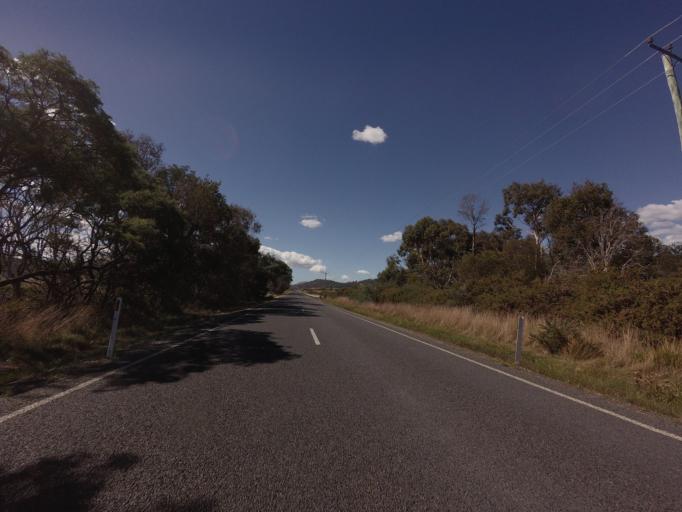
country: AU
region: Tasmania
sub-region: Break O'Day
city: St Helens
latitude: -41.6780
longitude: 147.8927
